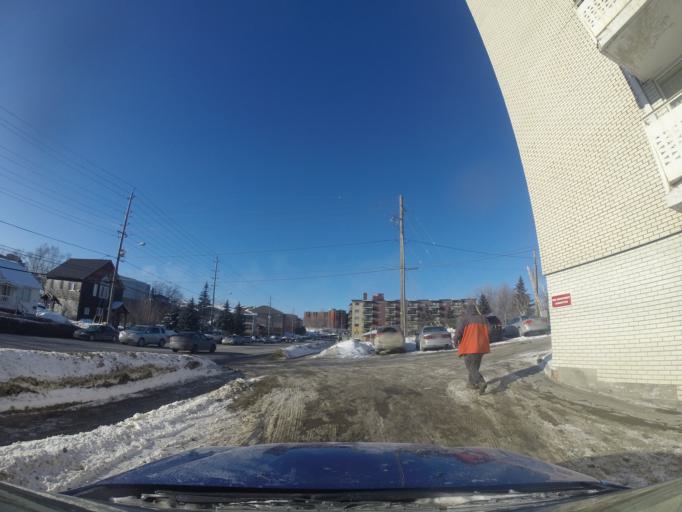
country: CA
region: Ontario
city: Greater Sudbury
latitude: 46.4563
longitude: -81.0009
